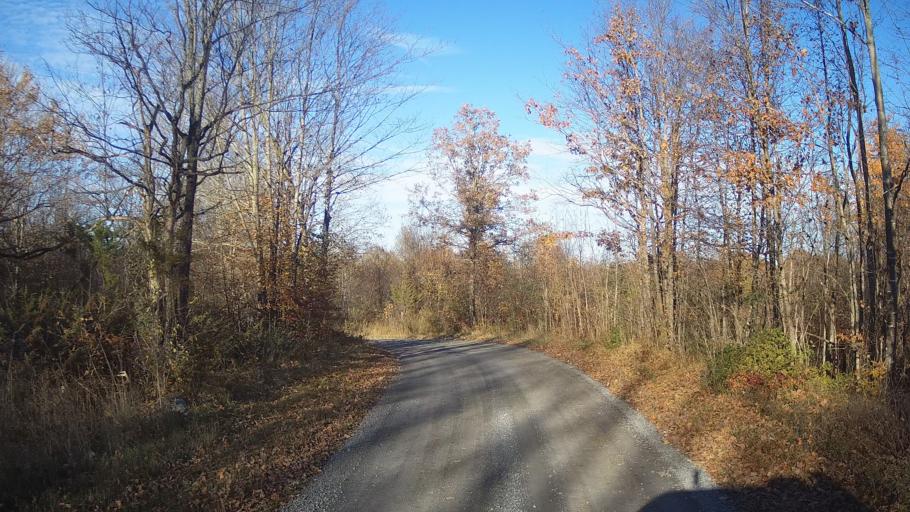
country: CA
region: Ontario
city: Perth
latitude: 44.7179
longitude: -76.4385
